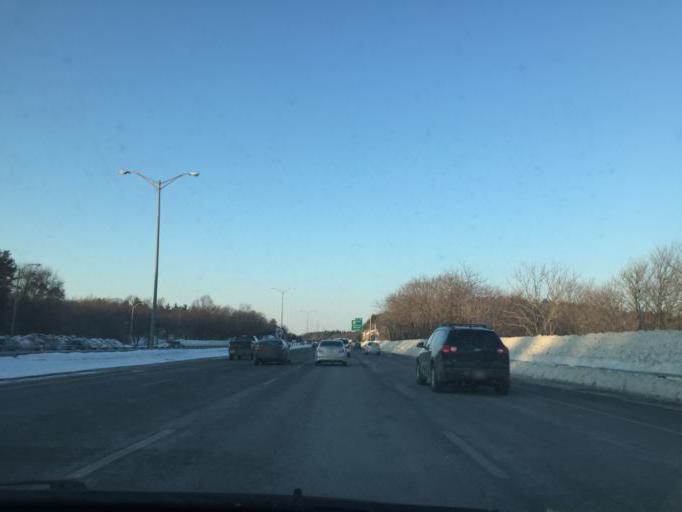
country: US
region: Massachusetts
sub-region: Middlesex County
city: Stoneham
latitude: 42.4499
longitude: -71.1041
